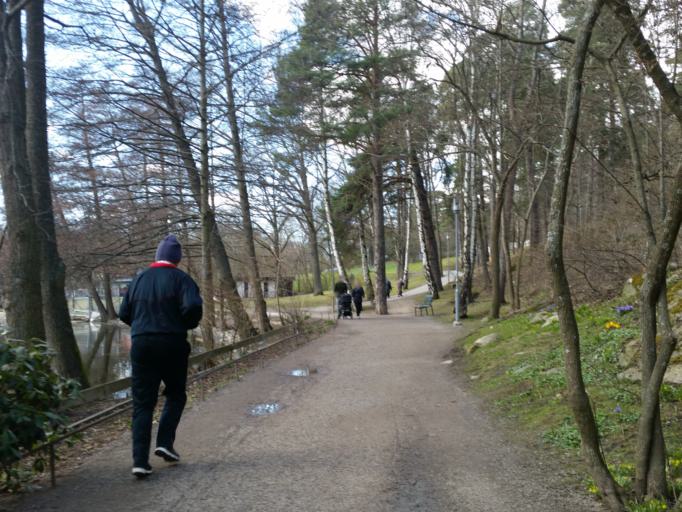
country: SE
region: Stockholm
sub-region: Sundbybergs Kommun
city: Sundbyberg
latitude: 59.3724
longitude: 17.9676
